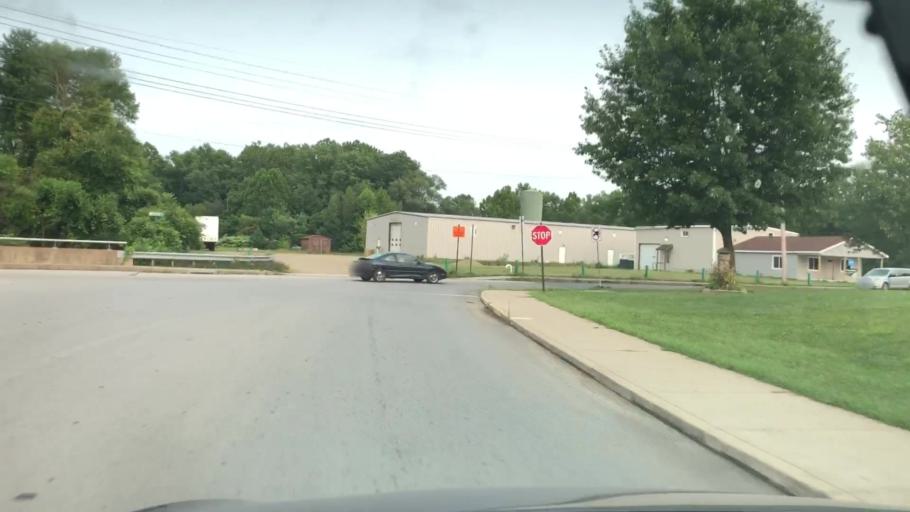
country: US
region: Pennsylvania
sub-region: Crawford County
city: Titusville
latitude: 41.6252
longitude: -79.6657
